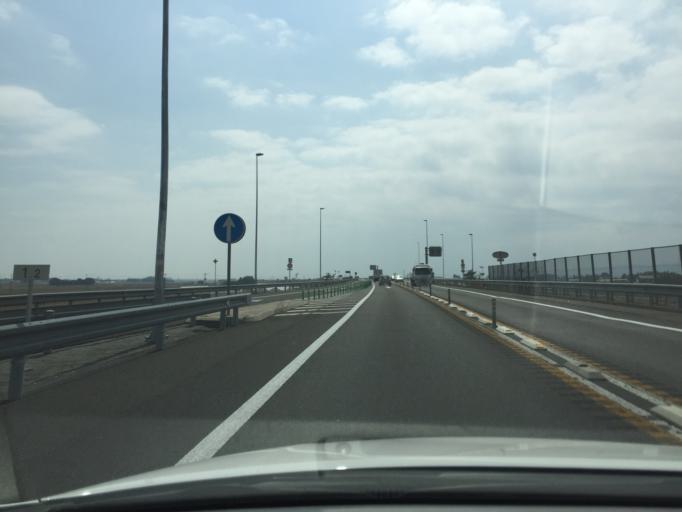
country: JP
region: Miyagi
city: Iwanuma
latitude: 38.0866
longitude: 140.8868
